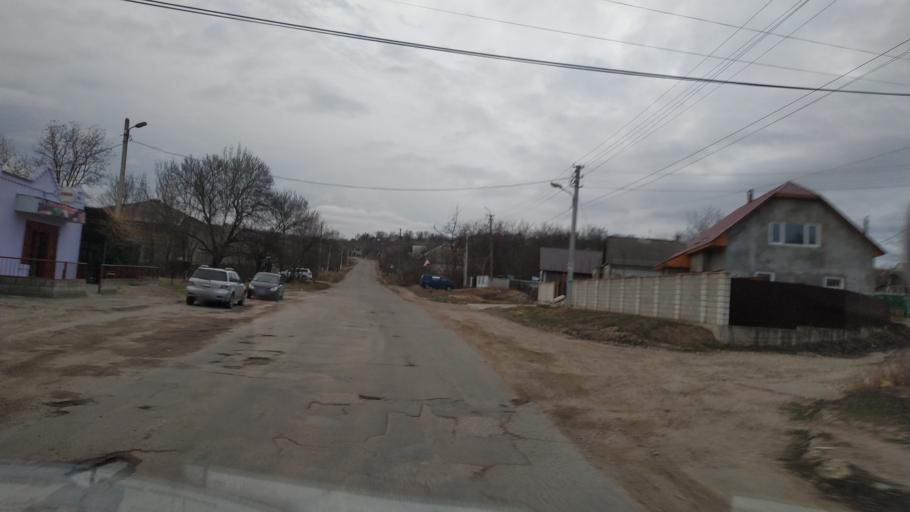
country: MD
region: Causeni
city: Causeni
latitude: 46.6336
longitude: 29.4032
